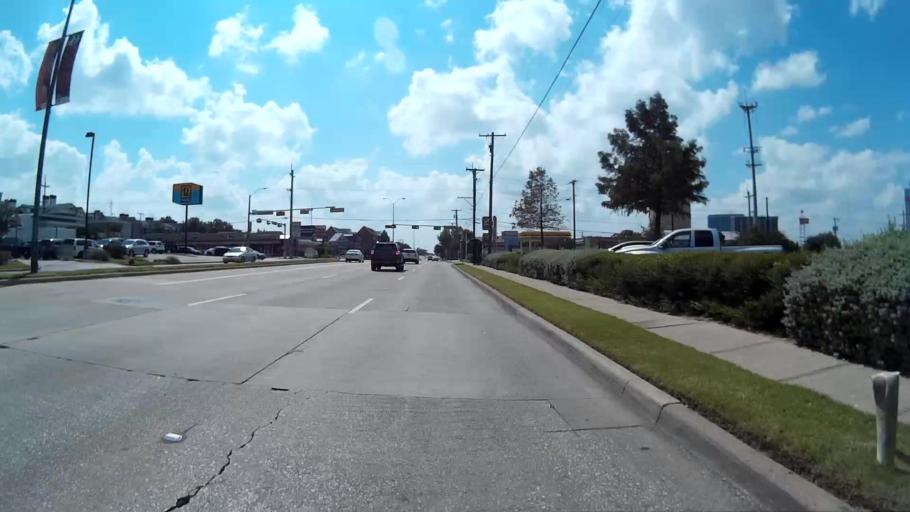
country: US
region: Texas
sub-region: Dallas County
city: Highland Park
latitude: 32.8464
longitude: -96.7702
